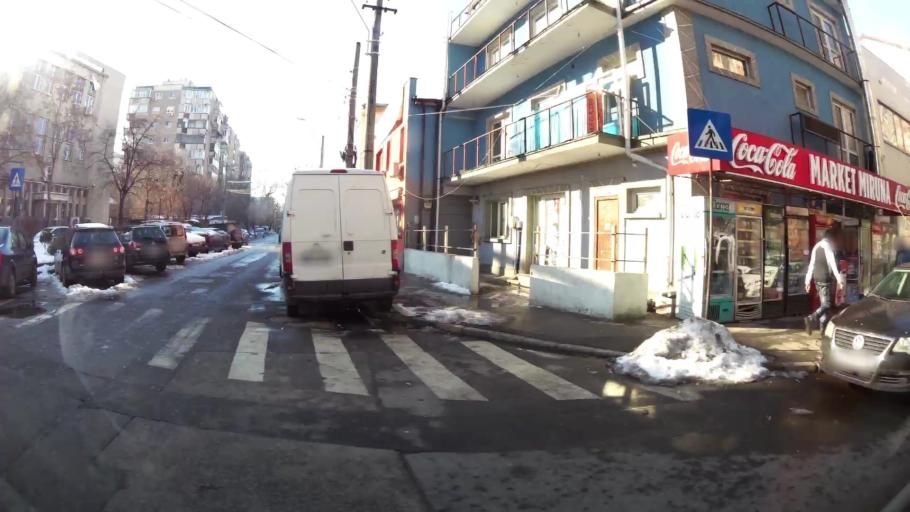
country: RO
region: Bucuresti
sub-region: Municipiul Bucuresti
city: Bucharest
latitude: 44.4623
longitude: 26.1264
